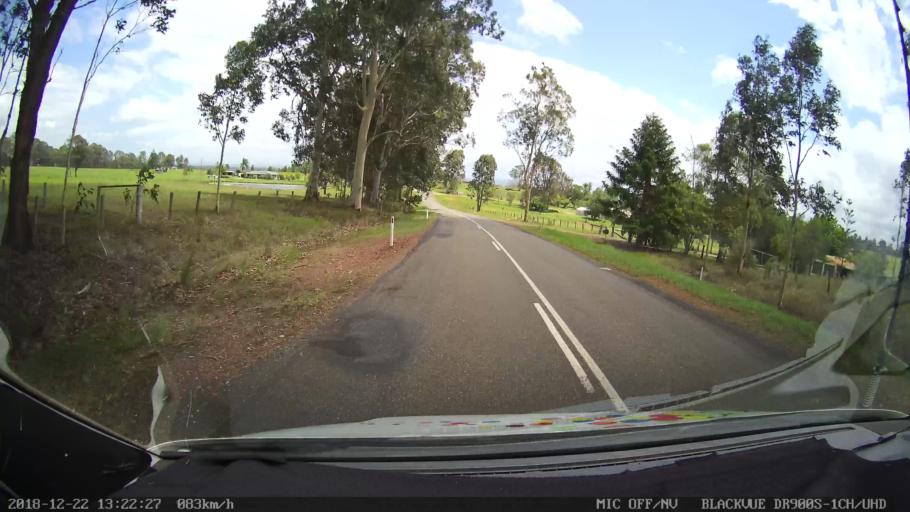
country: AU
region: New South Wales
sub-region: Clarence Valley
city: Coutts Crossing
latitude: -29.7868
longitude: 152.9116
